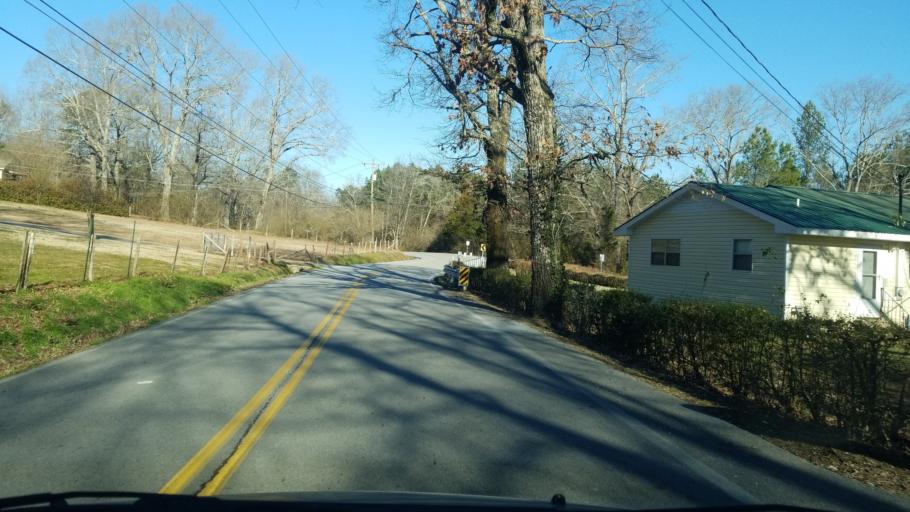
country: US
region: Tennessee
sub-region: Hamilton County
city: Collegedale
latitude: 35.0630
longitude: -85.0971
